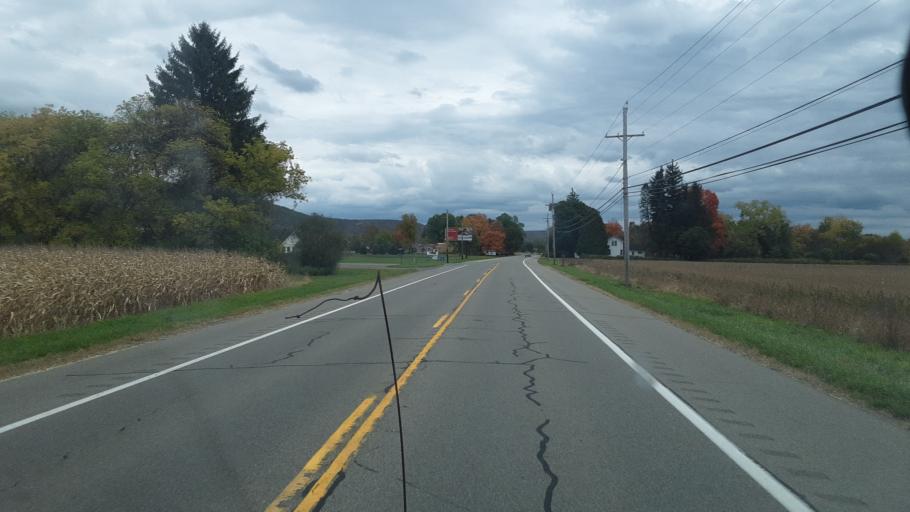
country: US
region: New York
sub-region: Allegany County
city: Belmont
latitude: 42.2044
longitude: -78.0080
